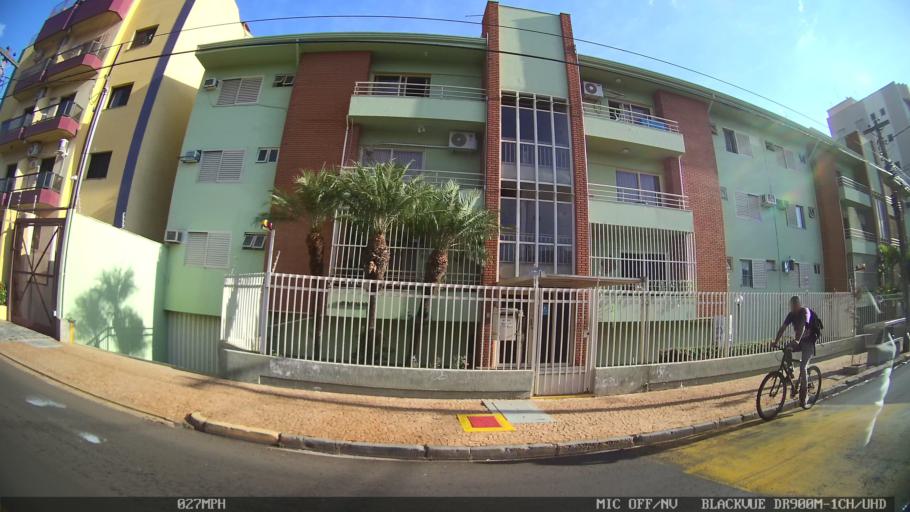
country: BR
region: Sao Paulo
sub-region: Ribeirao Preto
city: Ribeirao Preto
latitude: -21.1933
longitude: -47.7838
